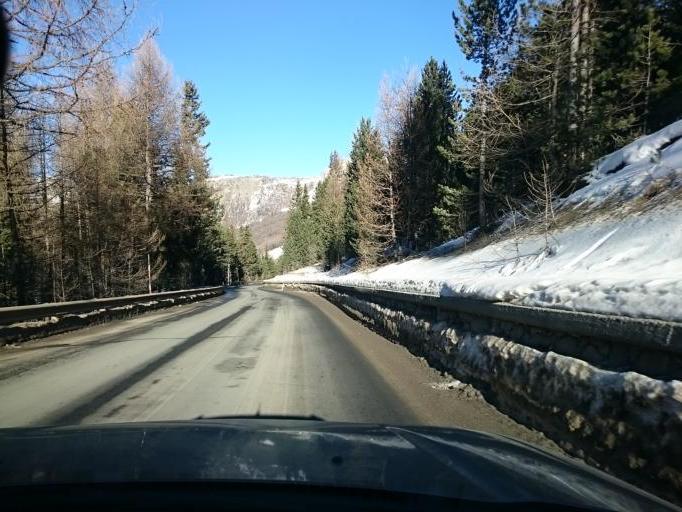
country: IT
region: Lombardy
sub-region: Provincia di Sondrio
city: Livigno
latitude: 46.5290
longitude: 10.1419
